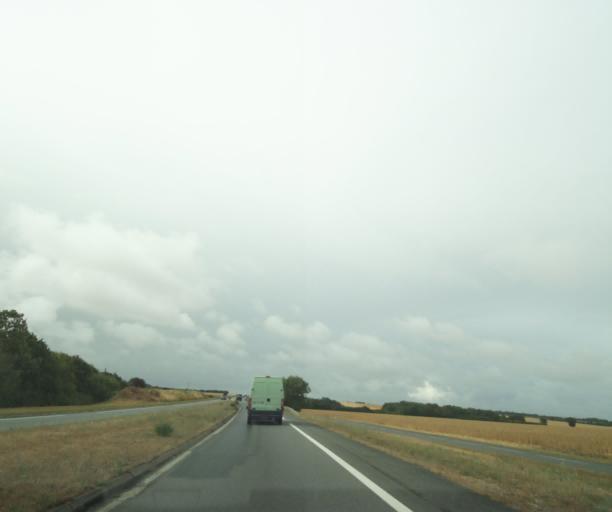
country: FR
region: Poitou-Charentes
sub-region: Departement de la Charente-Maritime
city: Marsilly
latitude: 46.2086
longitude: -1.1367
